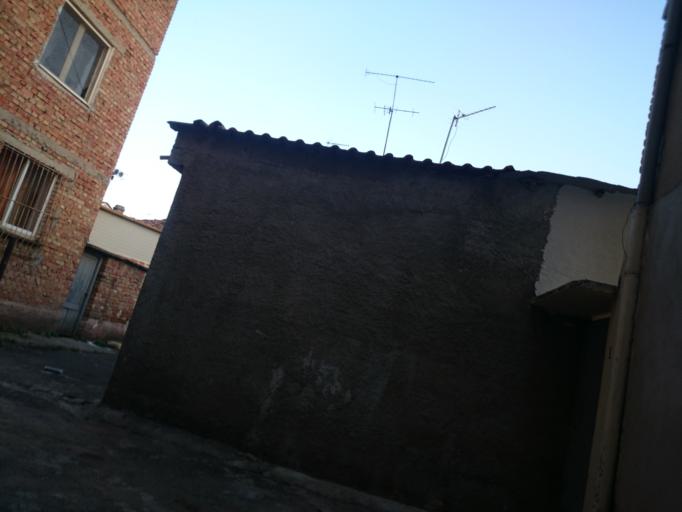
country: AL
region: Tirane
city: Tirana
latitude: 41.3276
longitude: 19.8069
